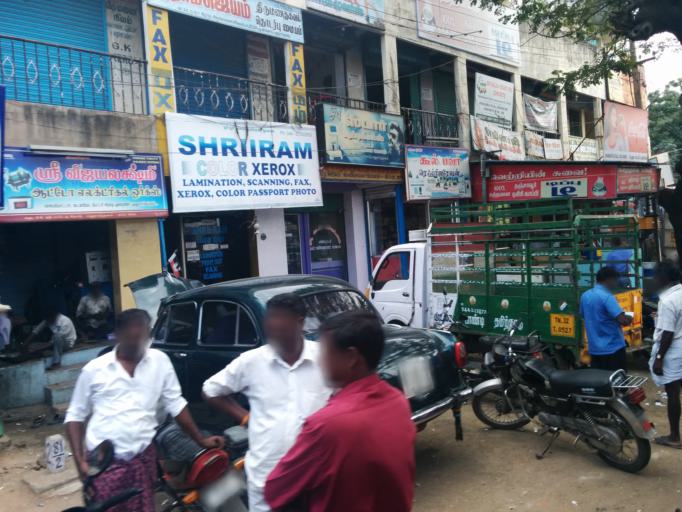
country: IN
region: Tamil Nadu
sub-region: Kancheepuram
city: Madurantakam
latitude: 12.5118
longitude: 79.8858
